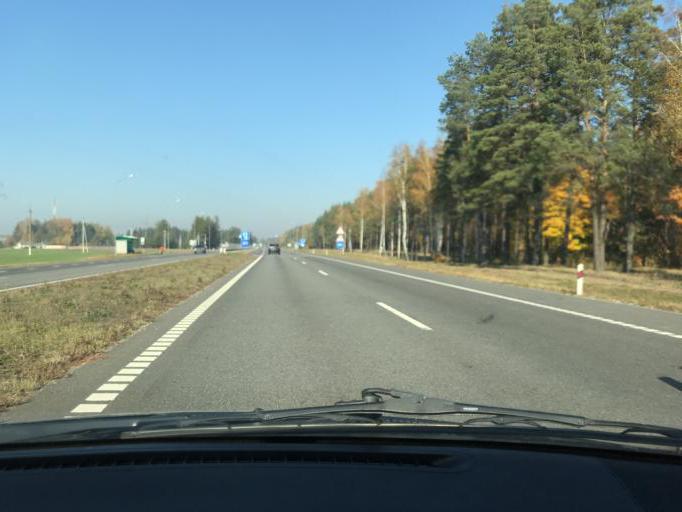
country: BY
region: Minsk
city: Slutsk
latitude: 53.3226
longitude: 27.5338
